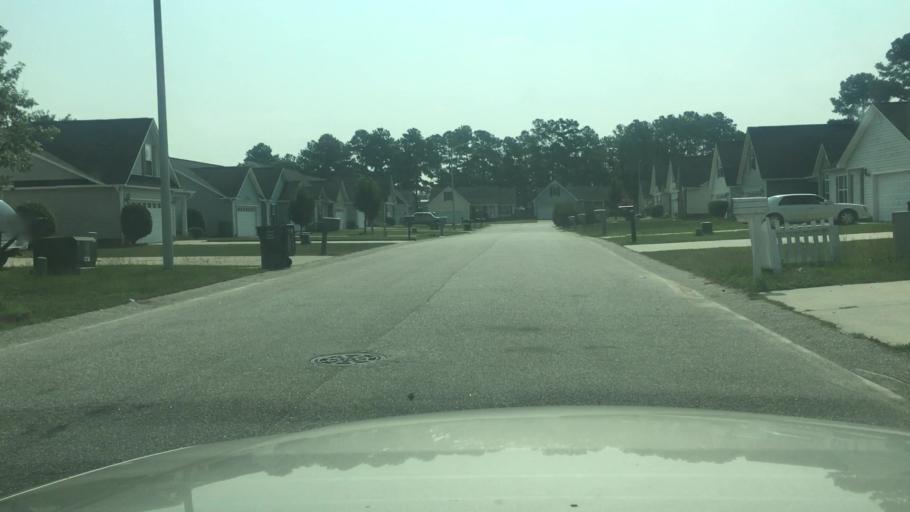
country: US
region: North Carolina
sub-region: Cumberland County
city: Hope Mills
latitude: 35.0004
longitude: -78.9432
